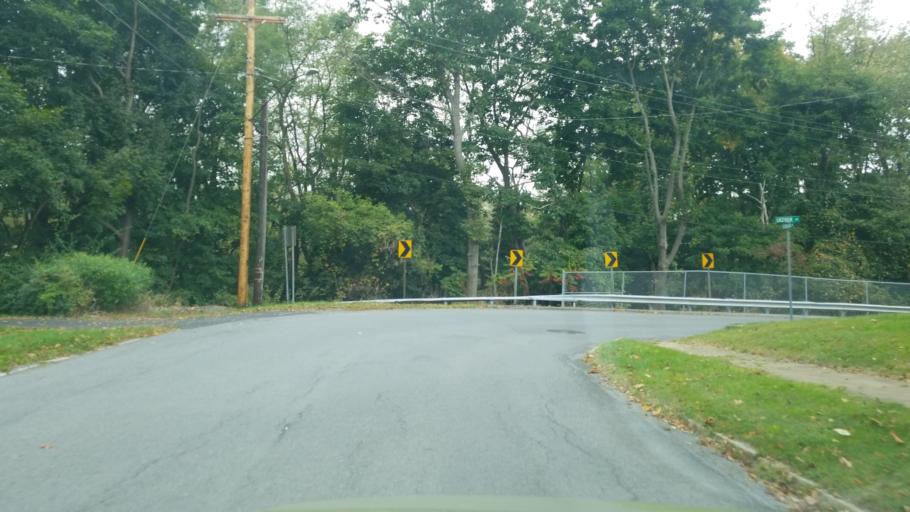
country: US
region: Pennsylvania
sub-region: Clearfield County
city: Curwensville
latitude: 40.9723
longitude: -78.5182
